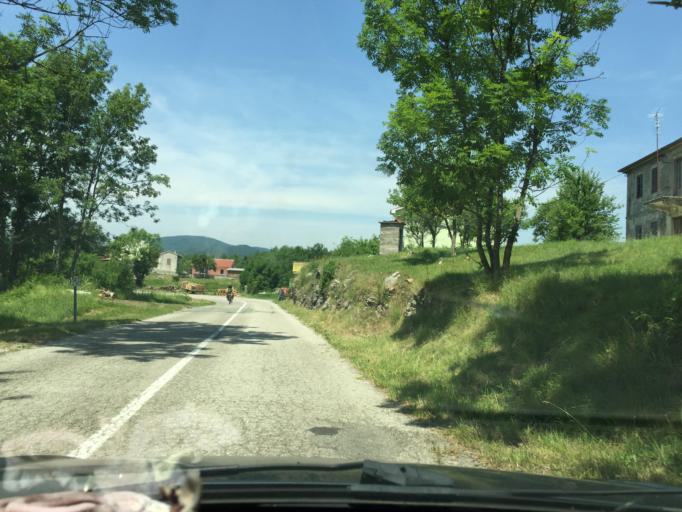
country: HR
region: Primorsko-Goranska
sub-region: Grad Opatija
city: Opatija
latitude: 45.4560
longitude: 14.1579
